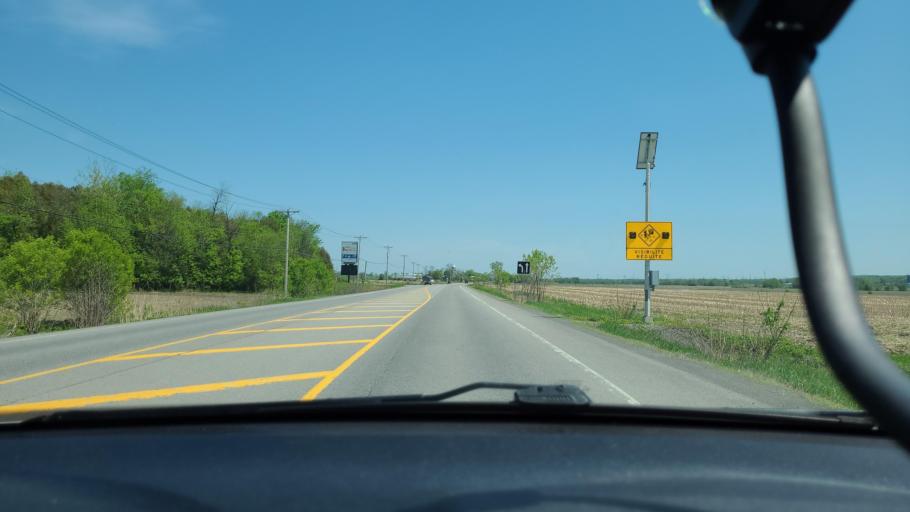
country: CA
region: Quebec
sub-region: Laurentides
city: Mirabel
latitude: 45.6182
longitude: -74.0973
